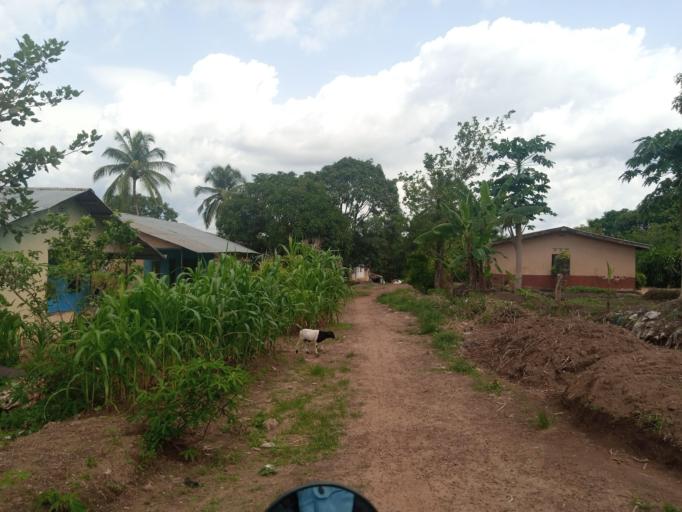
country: SL
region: Southern Province
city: Bo
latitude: 7.9812
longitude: -11.7295
